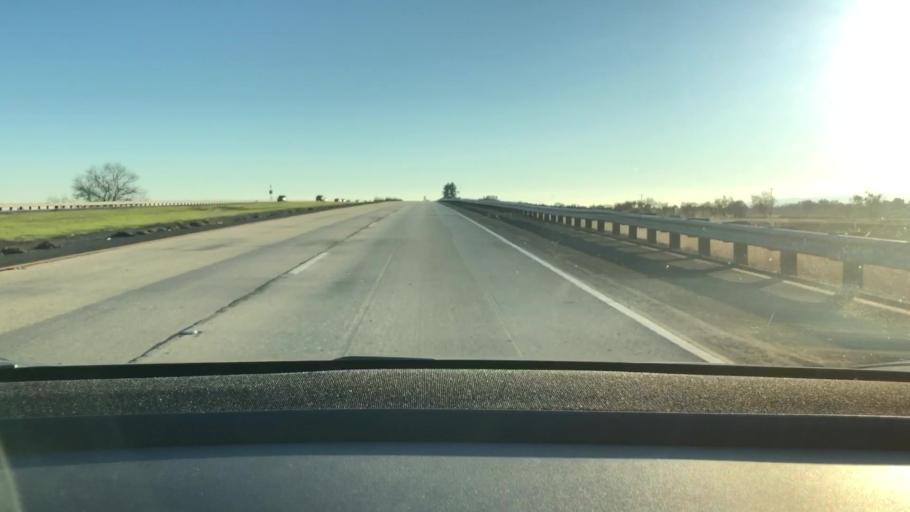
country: US
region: California
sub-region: Yolo County
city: Woodland
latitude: 38.6340
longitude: -121.7635
